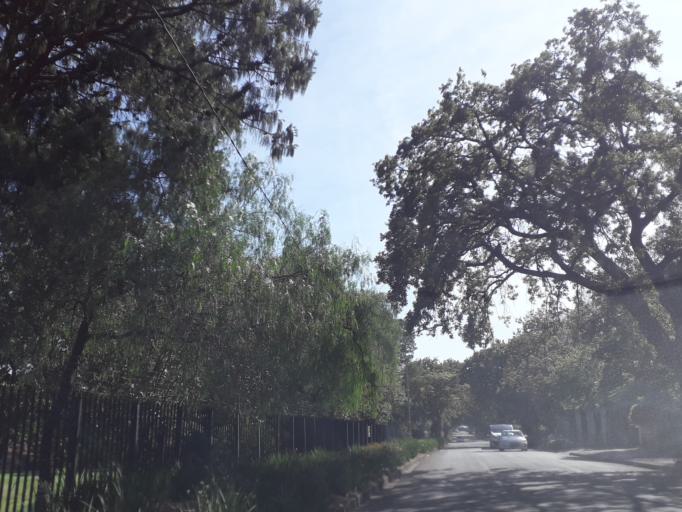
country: ZA
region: Gauteng
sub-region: City of Johannesburg Metropolitan Municipality
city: Johannesburg
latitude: -26.1772
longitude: 28.0600
